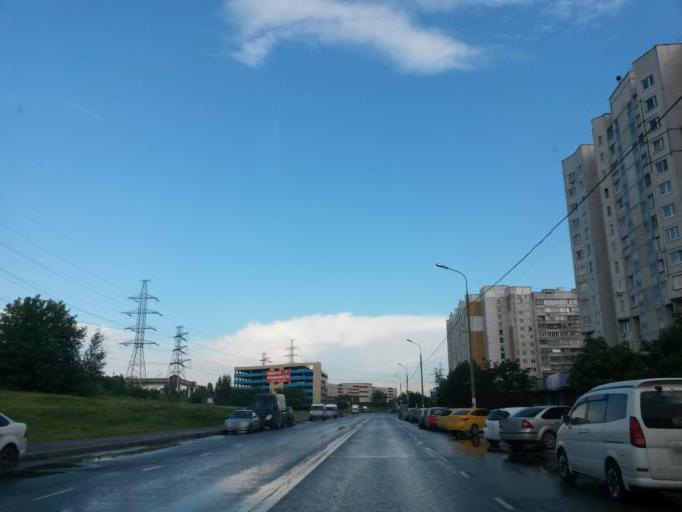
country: RU
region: Moscow
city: Annino
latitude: 55.5762
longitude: 37.5854
